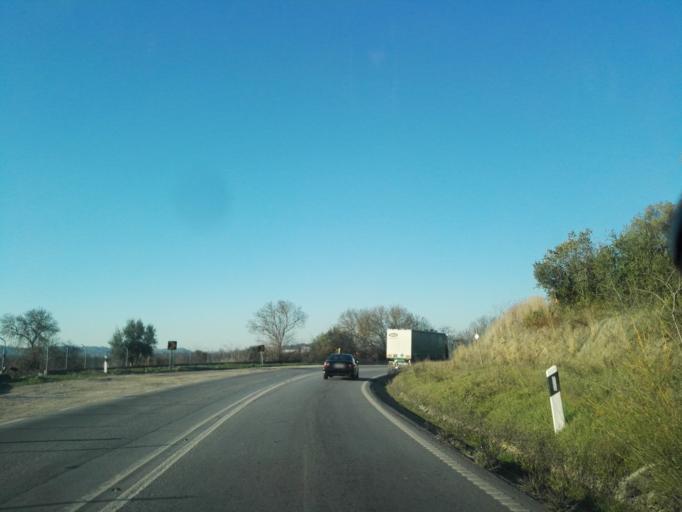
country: PT
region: Santarem
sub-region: Santarem
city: Santarem
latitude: 39.2077
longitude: -8.7090
